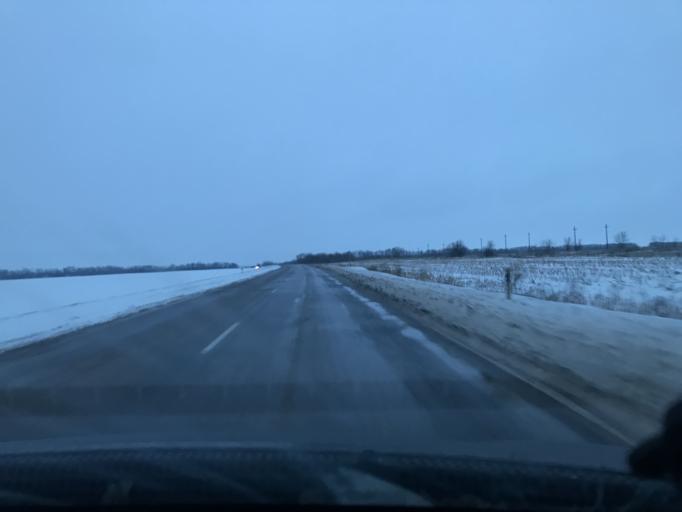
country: RU
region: Rostov
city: Letnik
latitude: 45.9891
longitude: 41.2278
